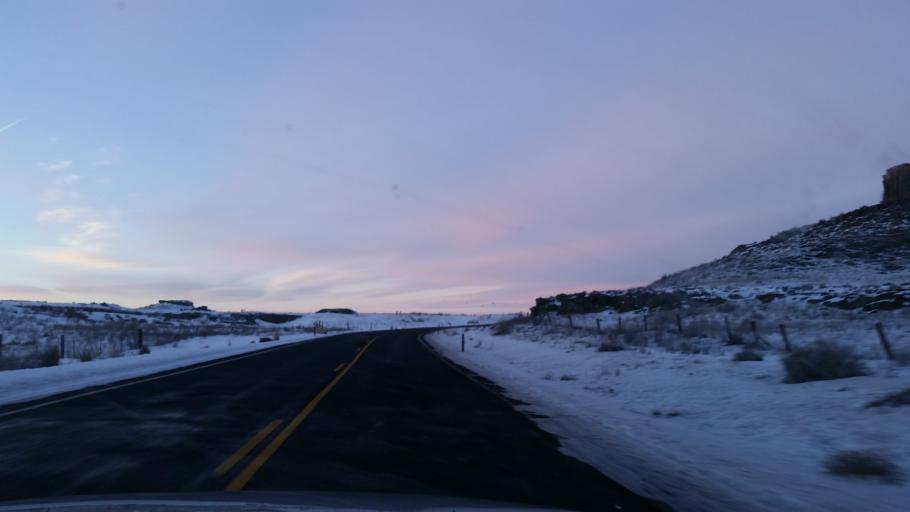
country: US
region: Washington
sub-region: Spokane County
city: Medical Lake
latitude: 47.2515
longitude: -117.9280
